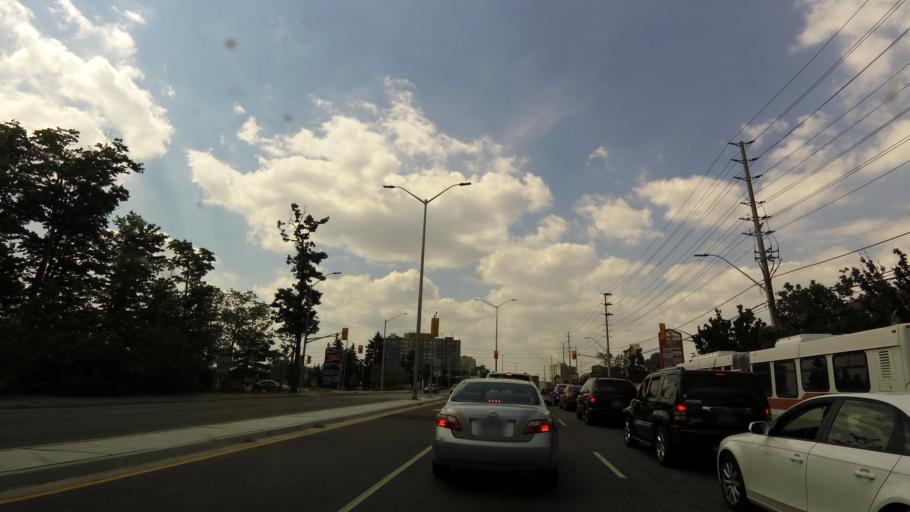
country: CA
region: Ontario
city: Etobicoke
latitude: 43.6212
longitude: -79.6008
